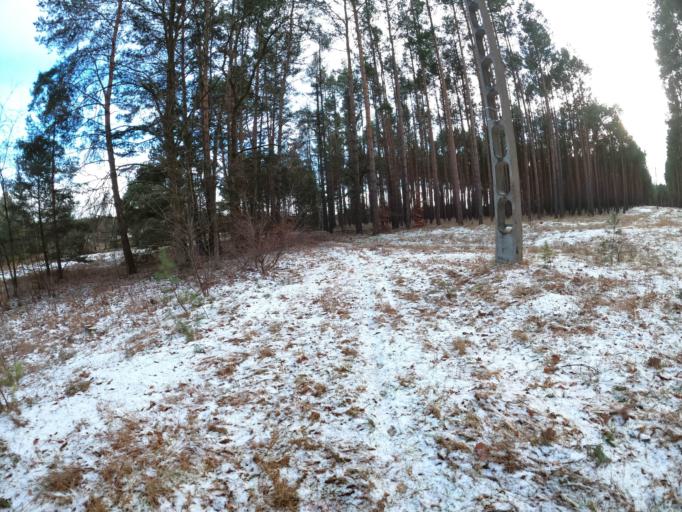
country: PL
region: Lubusz
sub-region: Powiat slubicki
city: Cybinka
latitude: 52.2176
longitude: 14.8385
